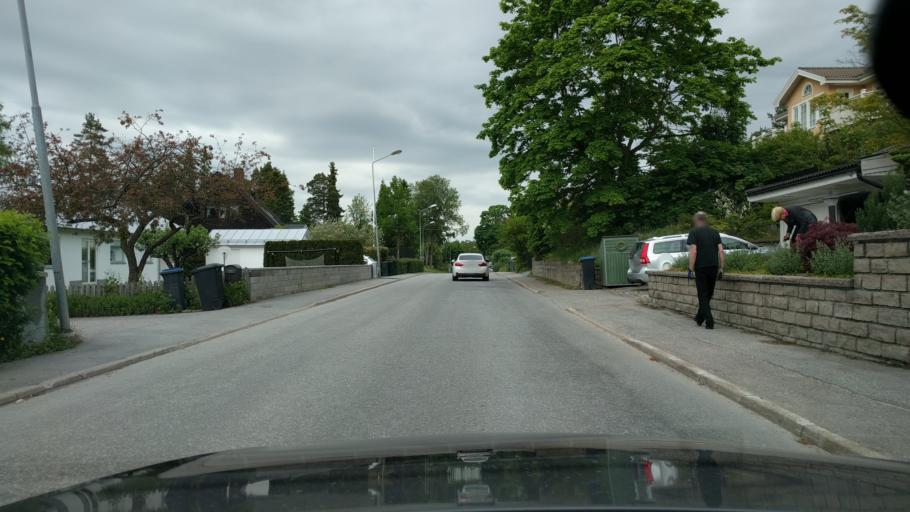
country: SE
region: Stockholm
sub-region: Taby Kommun
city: Taby
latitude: 59.4515
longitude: 18.0565
